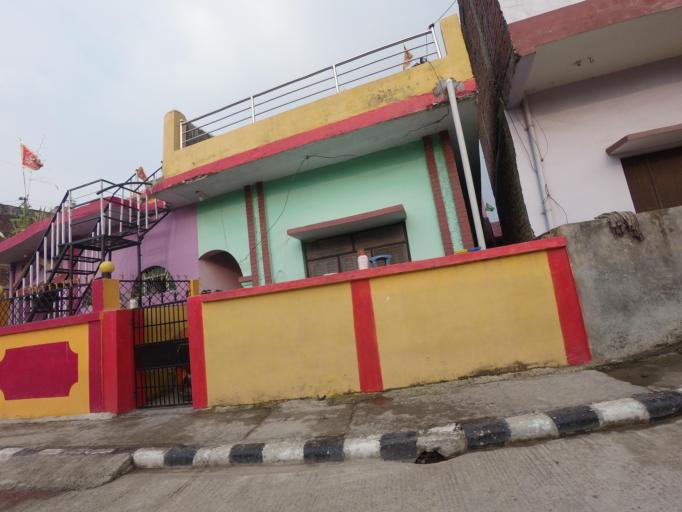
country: NP
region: Western Region
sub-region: Lumbini Zone
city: Bhairahawa
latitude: 27.5045
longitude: 83.4492
